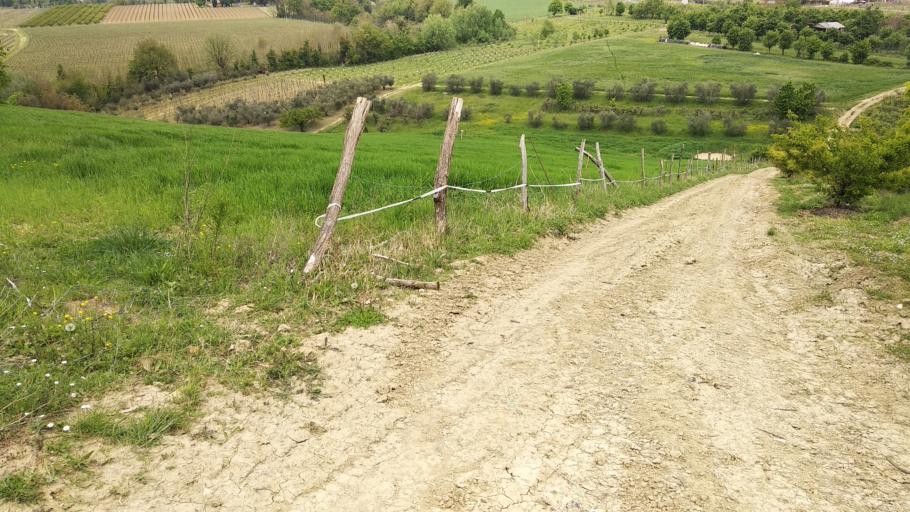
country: IT
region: Emilia-Romagna
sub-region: Provincia di Ravenna
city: Brisighella
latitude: 44.2032
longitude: 11.7622
